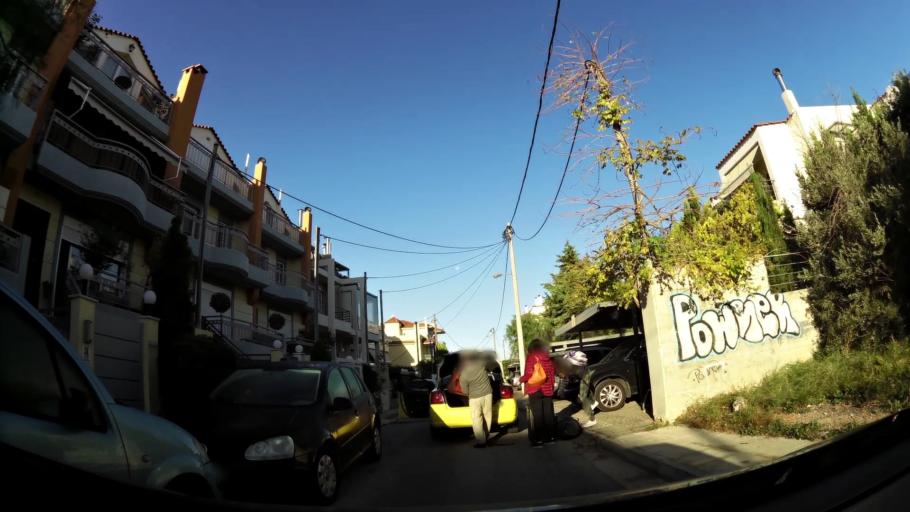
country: GR
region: Attica
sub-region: Nomarchia Anatolikis Attikis
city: Gerakas
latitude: 38.0250
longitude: 23.8449
